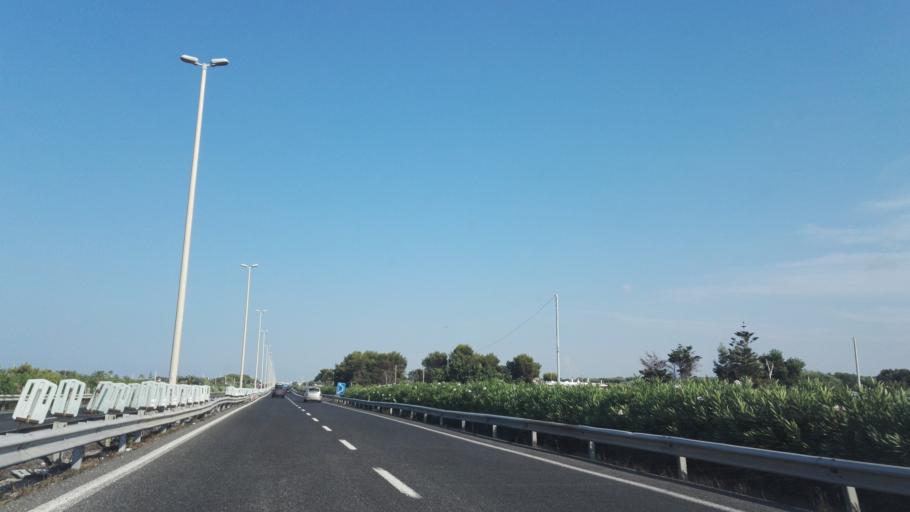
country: IT
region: Apulia
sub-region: Provincia di Bari
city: Mola di Bari
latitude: 41.0768
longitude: 17.0502
